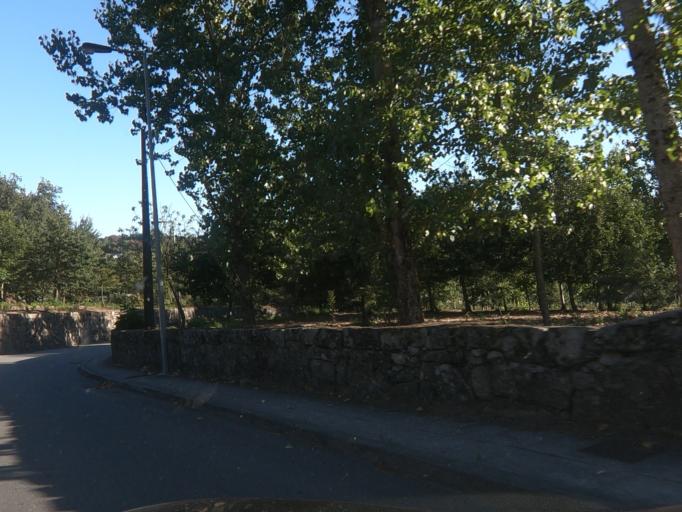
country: PT
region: Vila Real
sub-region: Vila Real
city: Vila Real
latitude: 41.3208
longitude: -7.7427
